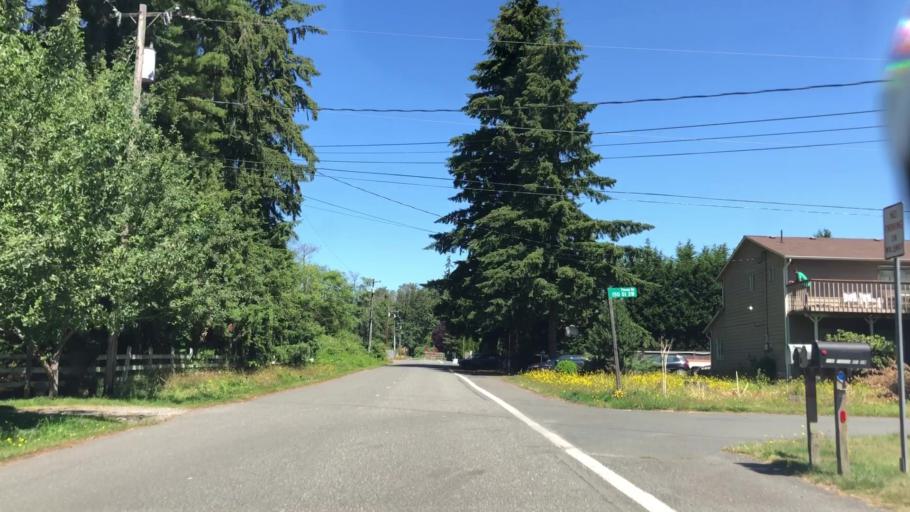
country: US
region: Washington
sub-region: Snohomish County
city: Martha Lake
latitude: 47.8614
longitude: -122.2360
